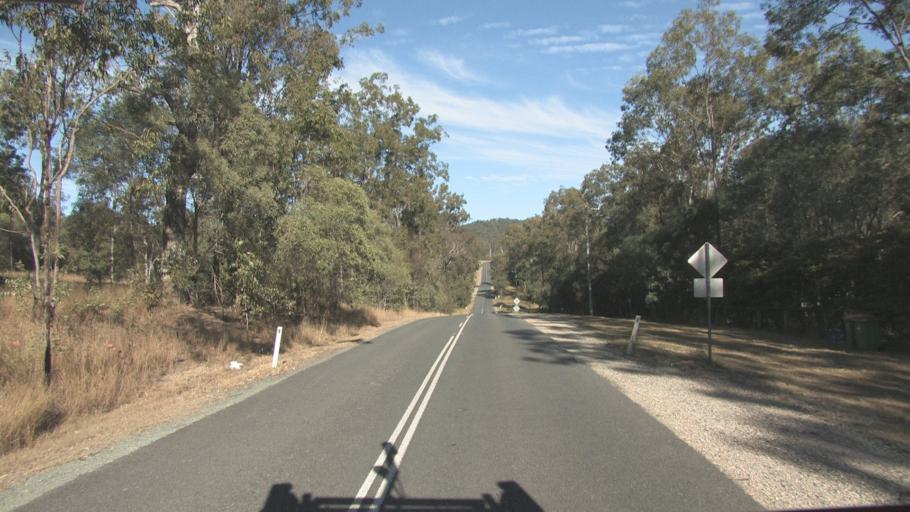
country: AU
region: Queensland
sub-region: Logan
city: Windaroo
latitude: -27.8126
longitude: 153.1697
